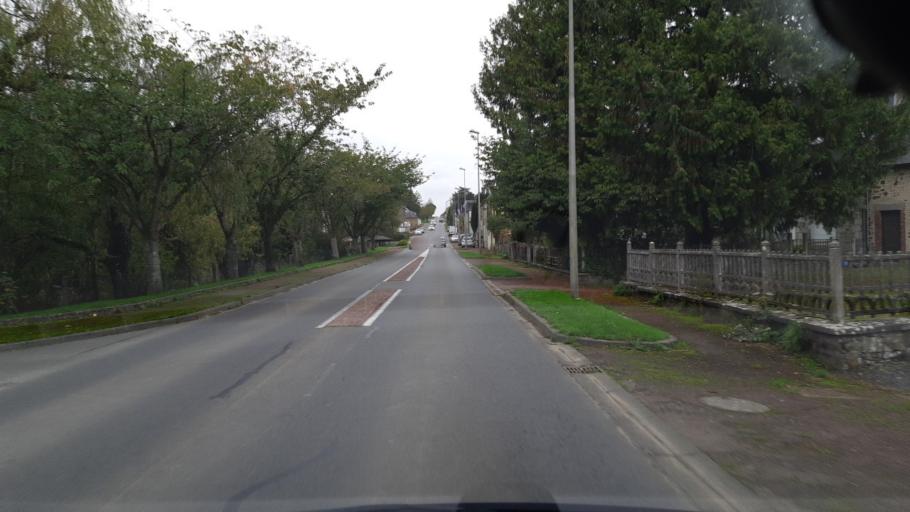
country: FR
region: Lower Normandy
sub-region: Departement de la Manche
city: Hambye
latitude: 48.9476
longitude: -1.2695
